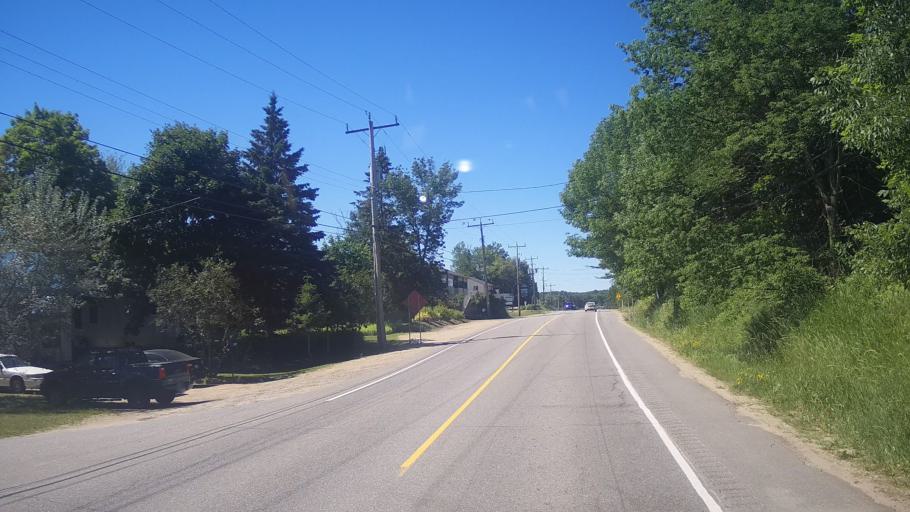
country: CA
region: Ontario
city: Huntsville
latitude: 45.3402
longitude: -79.2014
